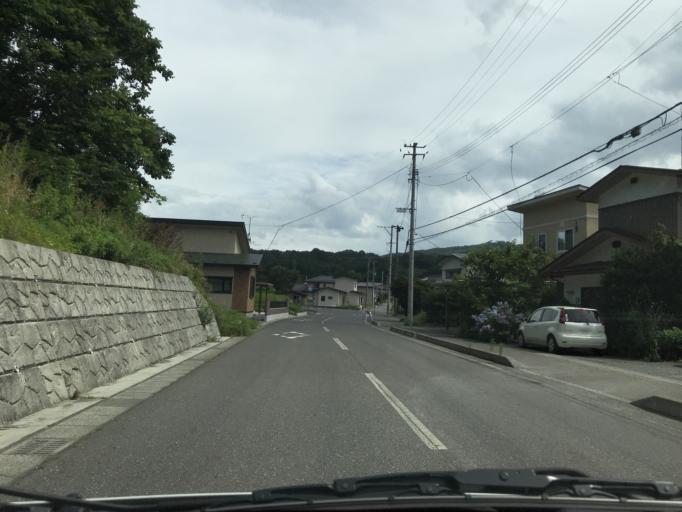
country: JP
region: Iwate
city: Tono
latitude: 39.3240
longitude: 141.5381
